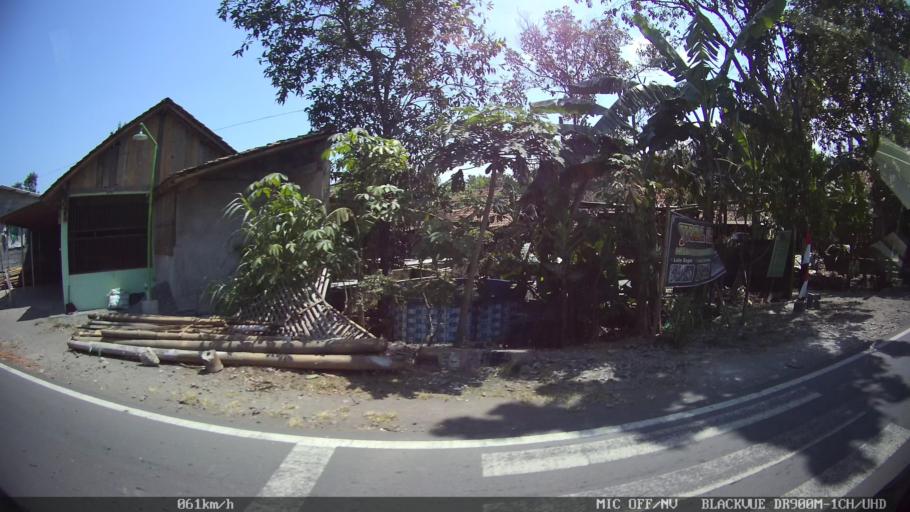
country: ID
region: Daerah Istimewa Yogyakarta
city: Srandakan
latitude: -7.9361
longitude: 110.2593
